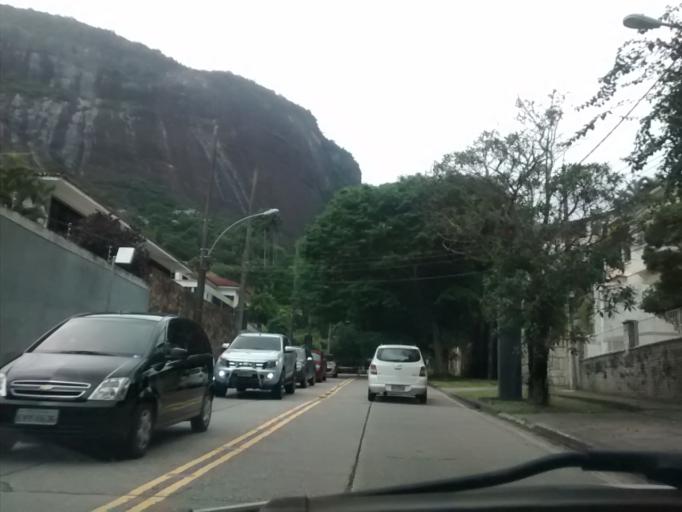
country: BR
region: Rio de Janeiro
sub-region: Rio De Janeiro
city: Rio de Janeiro
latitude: -22.9496
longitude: -43.2619
